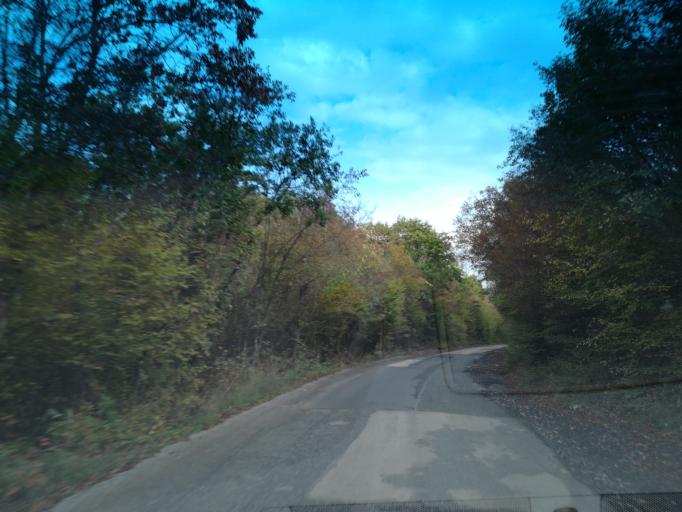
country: BG
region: Stara Zagora
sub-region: Obshtina Nikolaevo
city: Elkhovo
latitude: 42.3258
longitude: 25.3988
